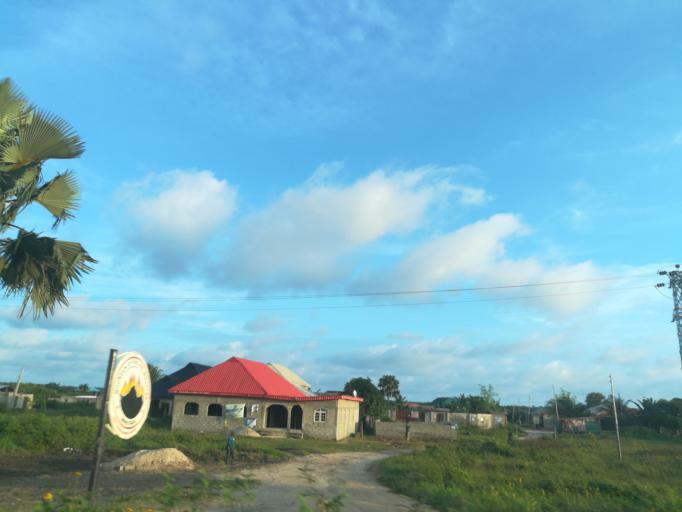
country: NG
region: Lagos
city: Badagry
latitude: 6.4692
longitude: 2.9846
